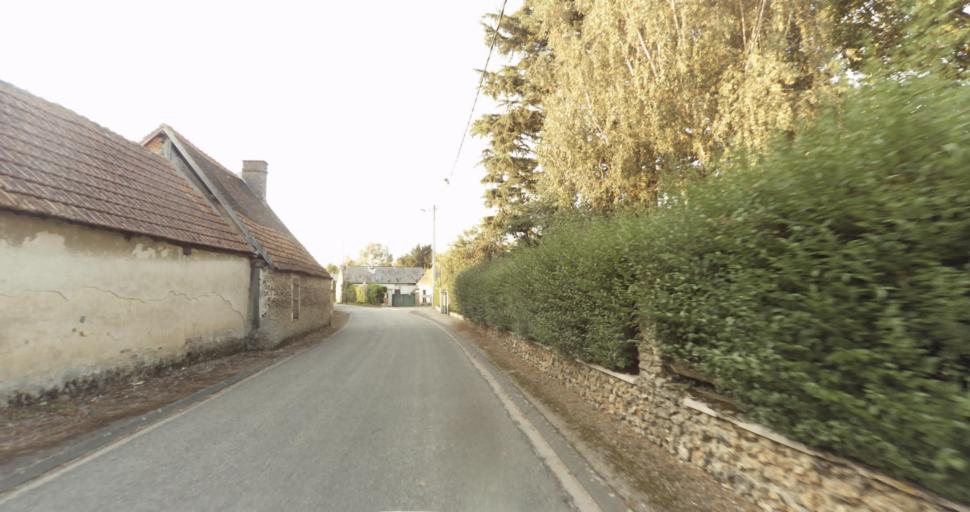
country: FR
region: Haute-Normandie
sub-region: Departement de l'Eure
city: Marcilly-sur-Eure
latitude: 48.8484
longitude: 1.2743
